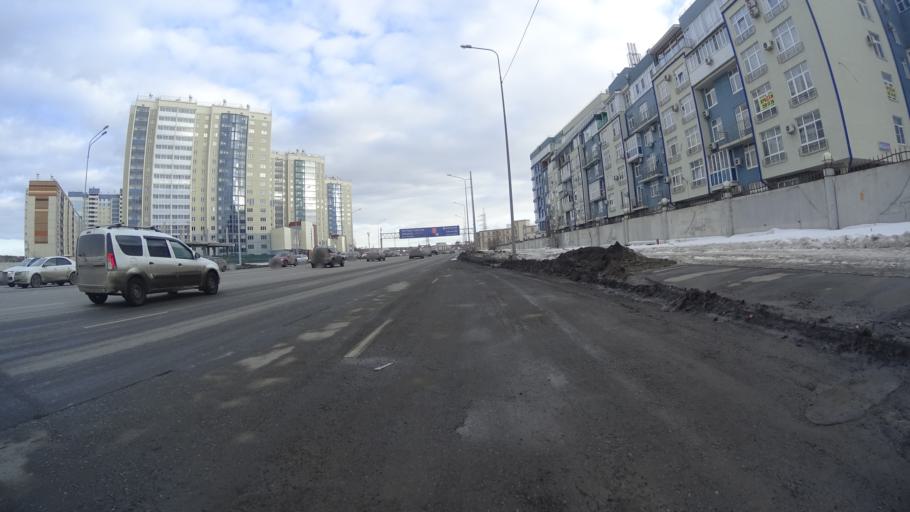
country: RU
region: Chelyabinsk
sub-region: Gorod Chelyabinsk
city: Chelyabinsk
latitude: 55.1597
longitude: 61.3027
